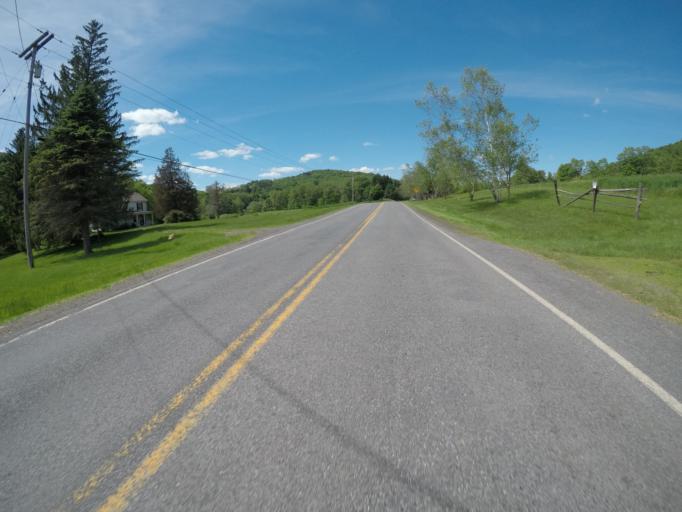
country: US
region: New York
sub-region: Delaware County
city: Delhi
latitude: 42.1770
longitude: -74.7898
